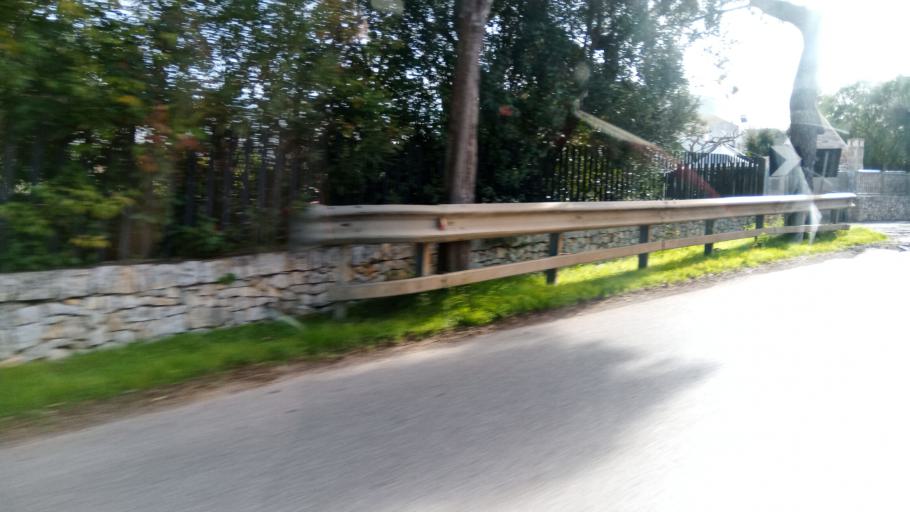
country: IT
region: Apulia
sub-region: Provincia di Bari
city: Castellana
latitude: 40.9002
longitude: 17.1668
